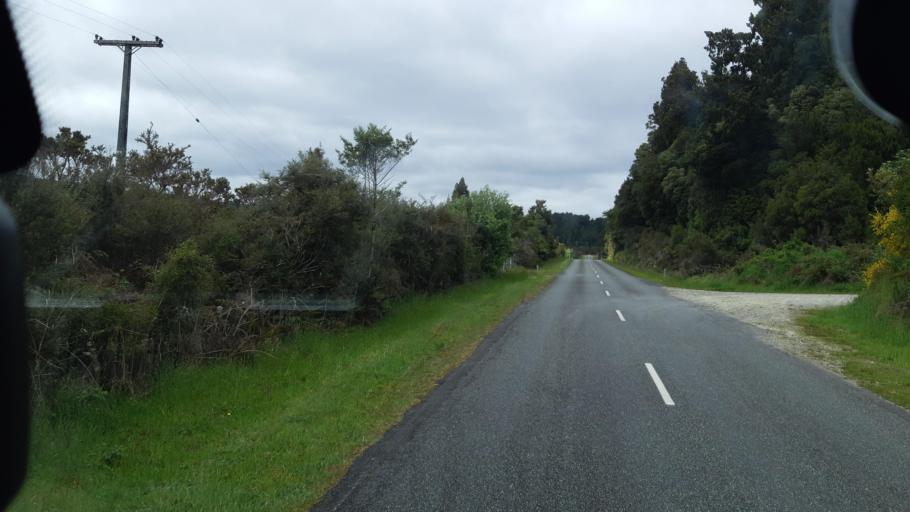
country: NZ
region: West Coast
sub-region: Westland District
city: Hokitika
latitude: -42.7720
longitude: 171.0827
